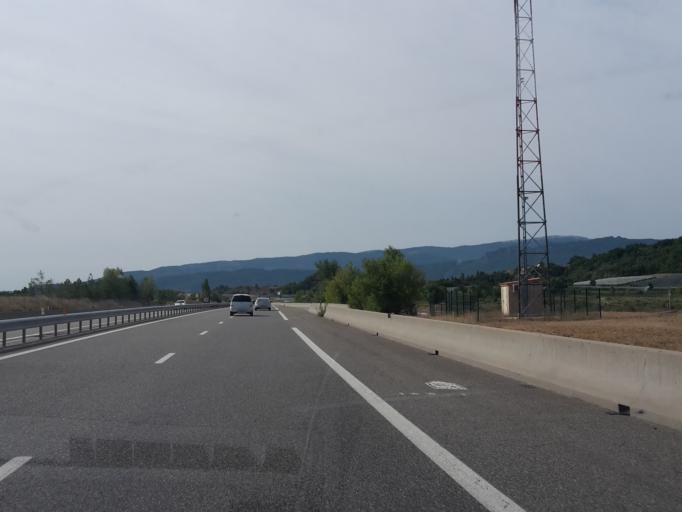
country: FR
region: Provence-Alpes-Cote d'Azur
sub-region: Departement des Hautes-Alpes
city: Laragne-Monteglin
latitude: 44.3081
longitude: 5.9002
